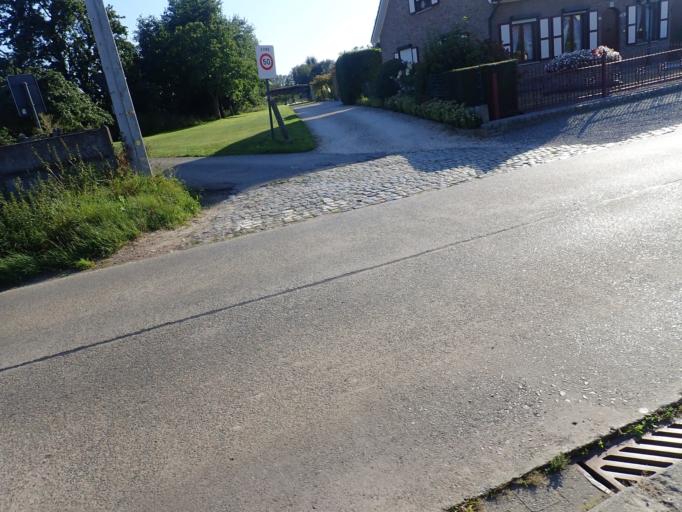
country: BE
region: Flanders
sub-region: Provincie Antwerpen
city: Heist-op-den-Berg
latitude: 51.1006
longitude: 4.7442
